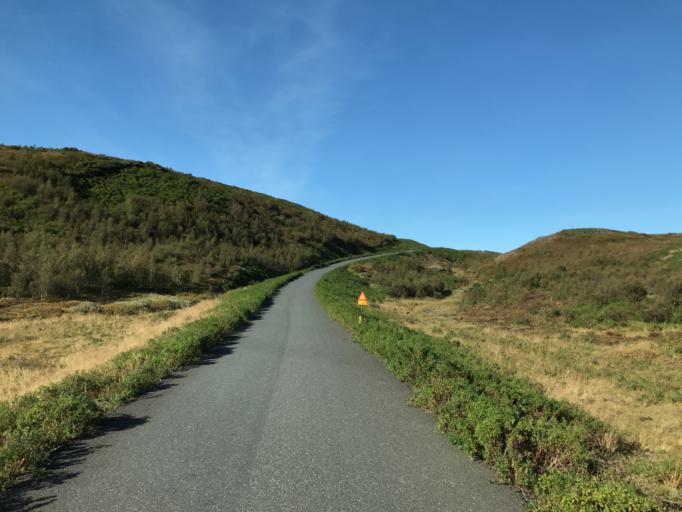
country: IS
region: South
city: Hveragerdi
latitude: 64.1290
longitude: -21.2505
